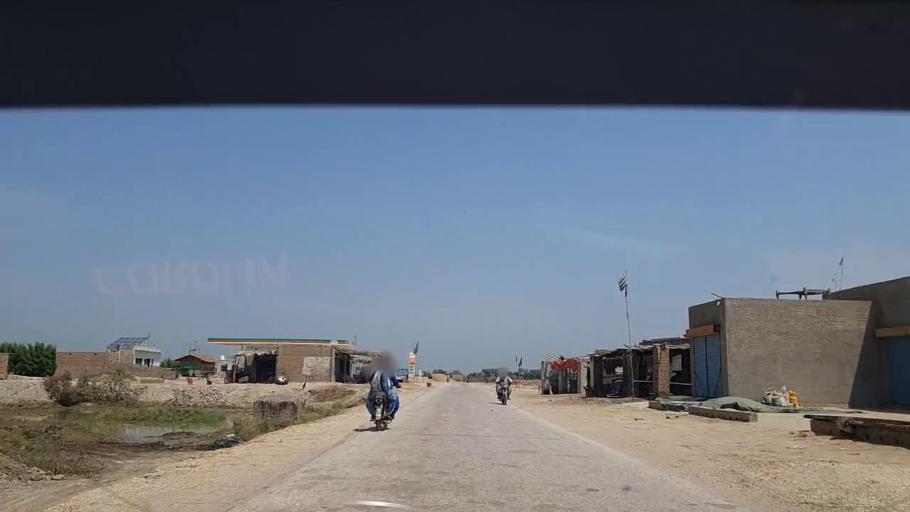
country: PK
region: Sindh
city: Thul
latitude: 28.1240
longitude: 68.8168
